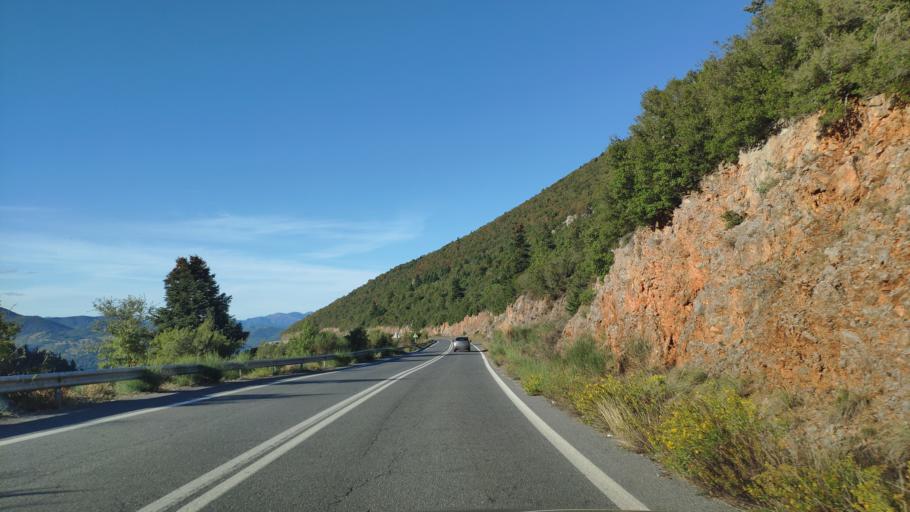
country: GR
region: Peloponnese
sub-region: Nomos Arkadias
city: Langadhia
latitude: 37.7017
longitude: 22.1977
